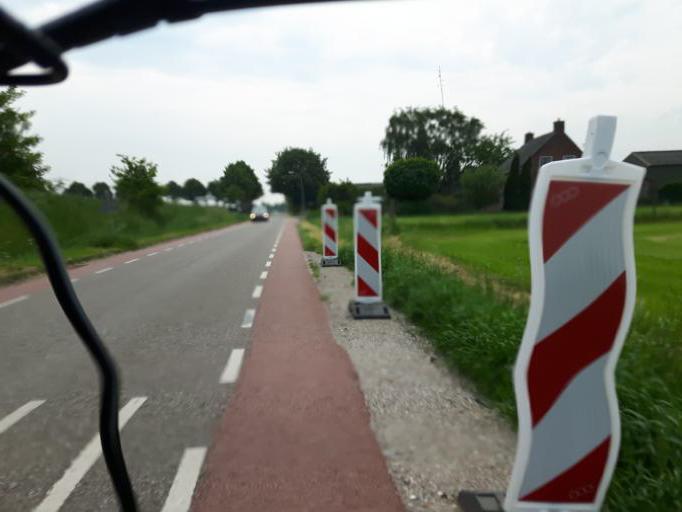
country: NL
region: North Brabant
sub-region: Gemeente Steenbergen
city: Welberg
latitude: 51.5511
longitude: 4.3346
